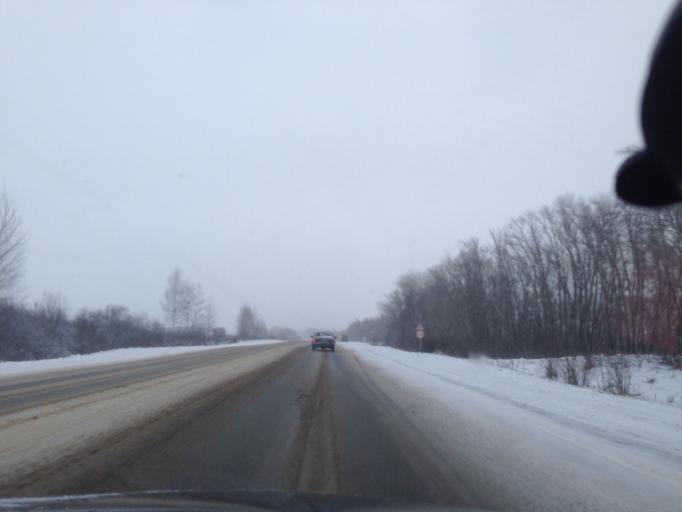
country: RU
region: Tula
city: Bolokhovo
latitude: 54.0828
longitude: 37.7789
